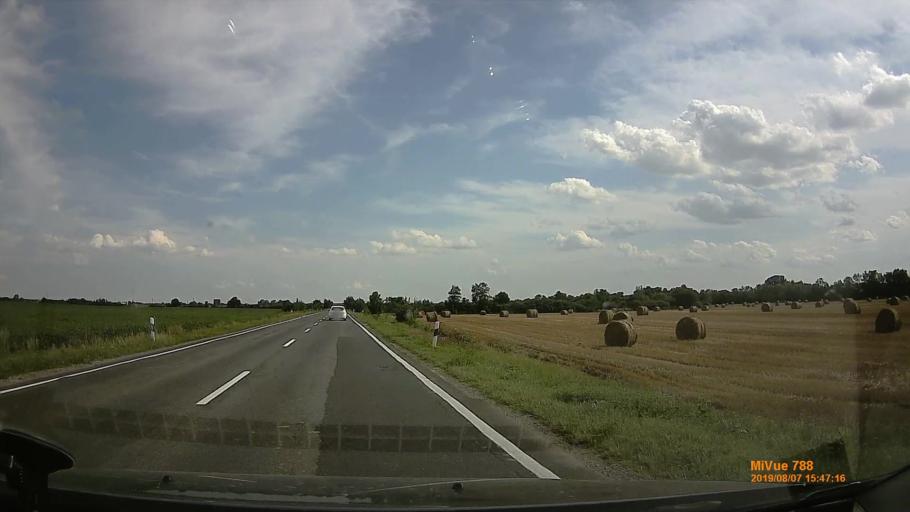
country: HU
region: Vas
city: Jak
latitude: 47.1736
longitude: 16.6257
